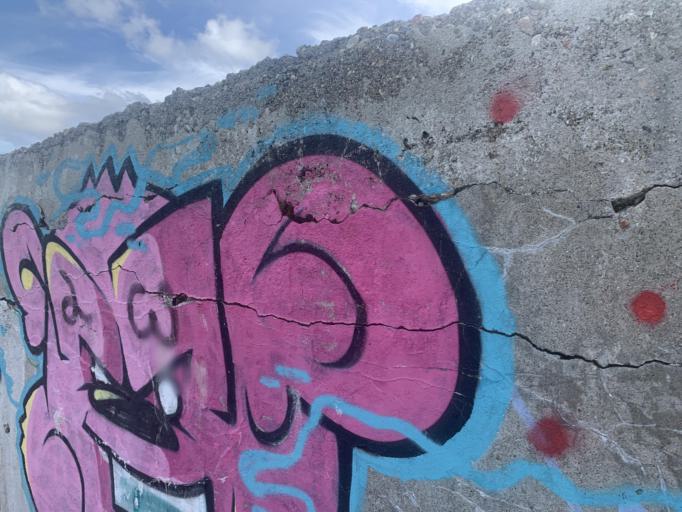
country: RU
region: Murmansk
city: Monchegorsk
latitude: 67.9164
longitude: 32.9780
